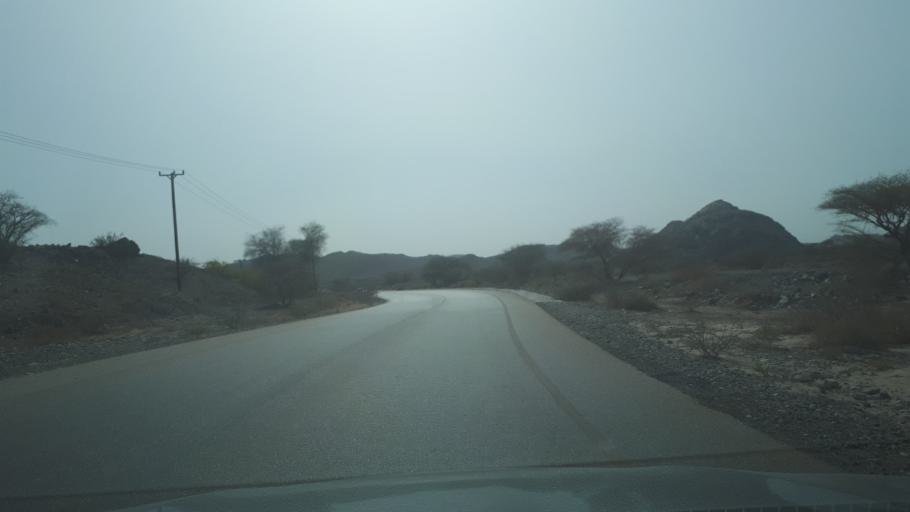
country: OM
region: Az Zahirah
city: `Ibri
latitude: 23.1462
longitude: 56.9009
